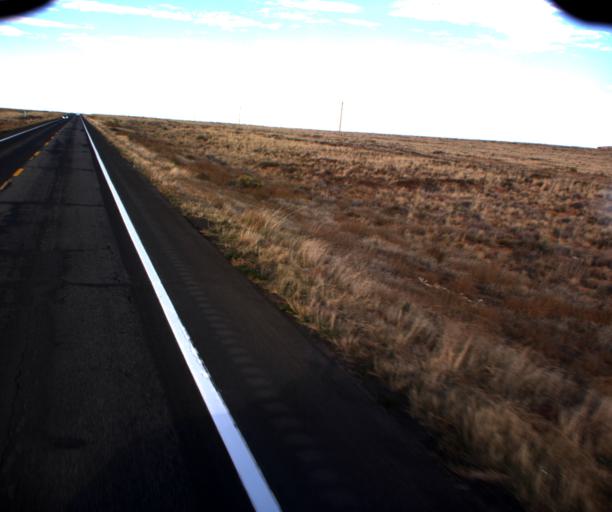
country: US
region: Arizona
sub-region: Apache County
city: Lukachukai
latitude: 36.9585
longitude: -109.3127
